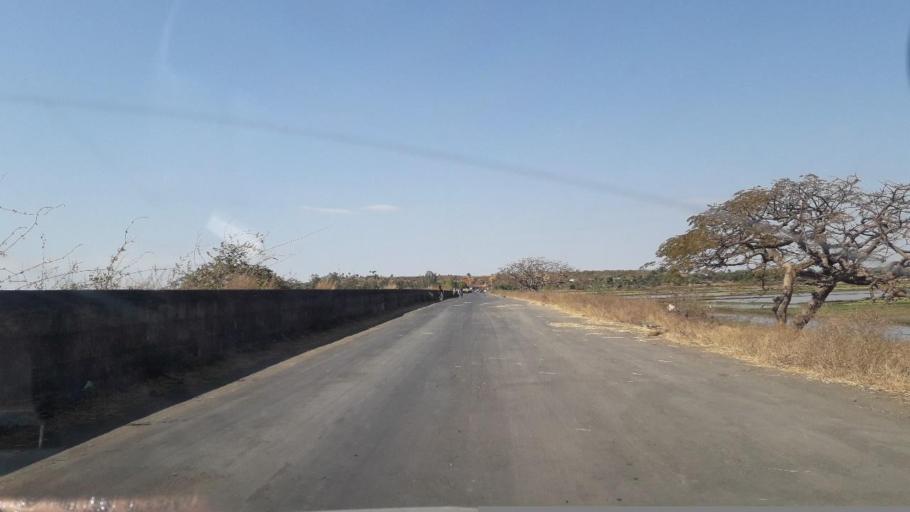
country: MG
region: Boeny
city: Marovoay
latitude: -16.1287
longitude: 46.7475
